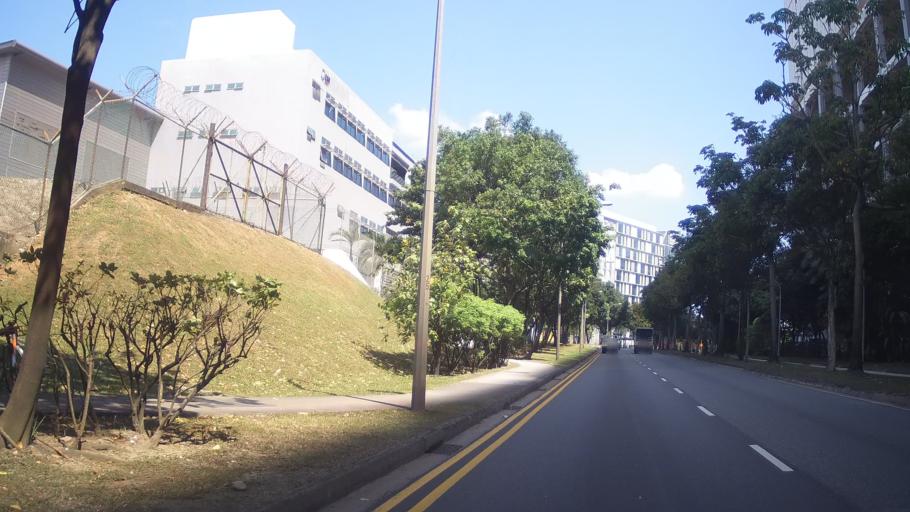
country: SG
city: Singapore
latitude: 1.3115
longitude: 103.6966
